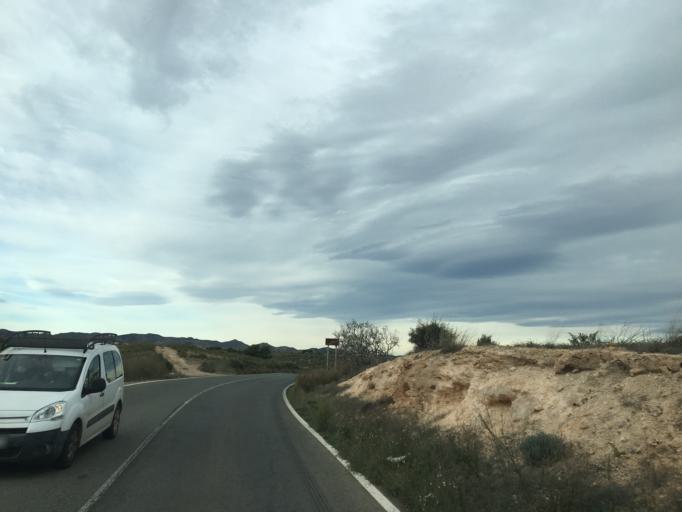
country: ES
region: Murcia
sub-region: Murcia
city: Cartagena
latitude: 37.6154
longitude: -1.0640
